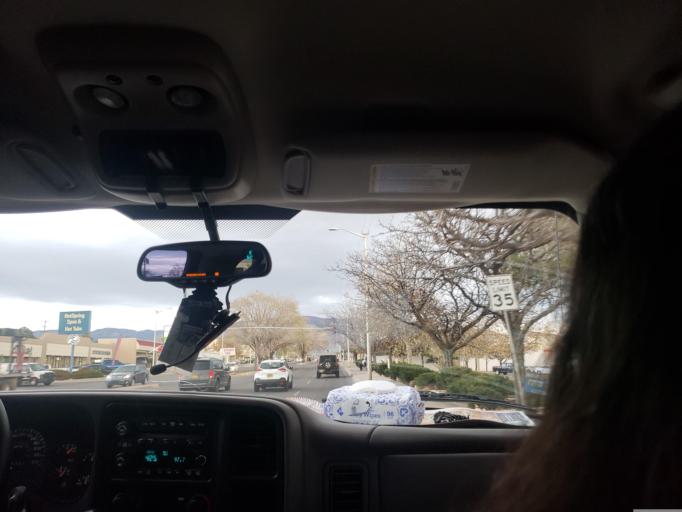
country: US
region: New Mexico
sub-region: Bernalillo County
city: North Valley
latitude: 35.1105
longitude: -106.5779
